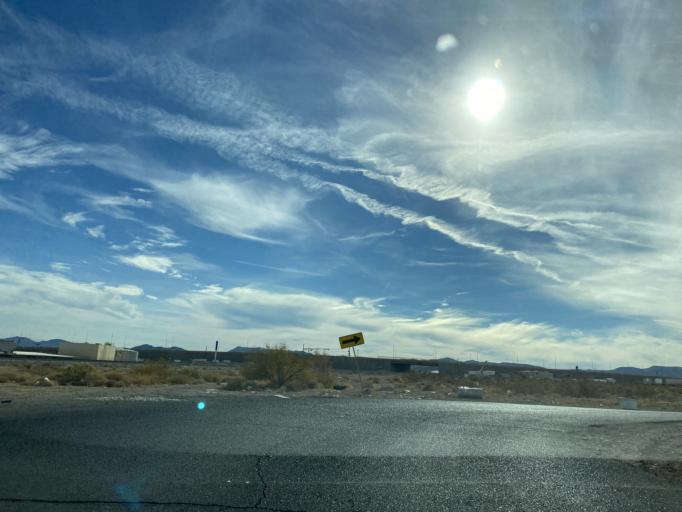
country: US
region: Nevada
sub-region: Clark County
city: Enterprise
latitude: 36.0297
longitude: -115.2258
